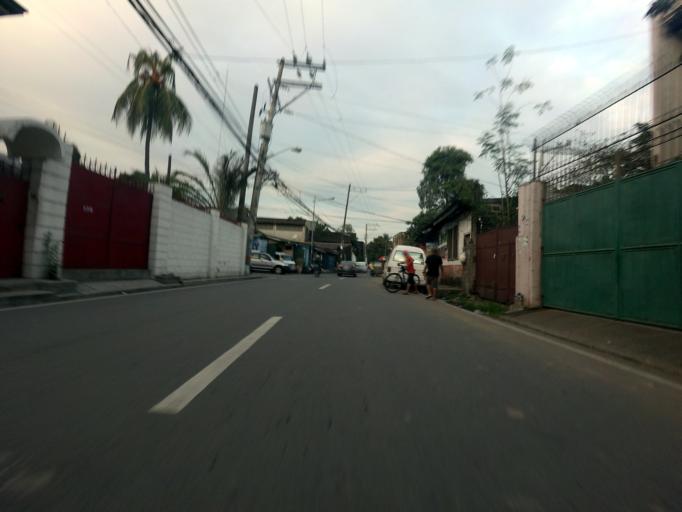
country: PH
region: Metro Manila
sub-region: San Juan
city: San Juan
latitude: 14.5980
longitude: 121.0325
